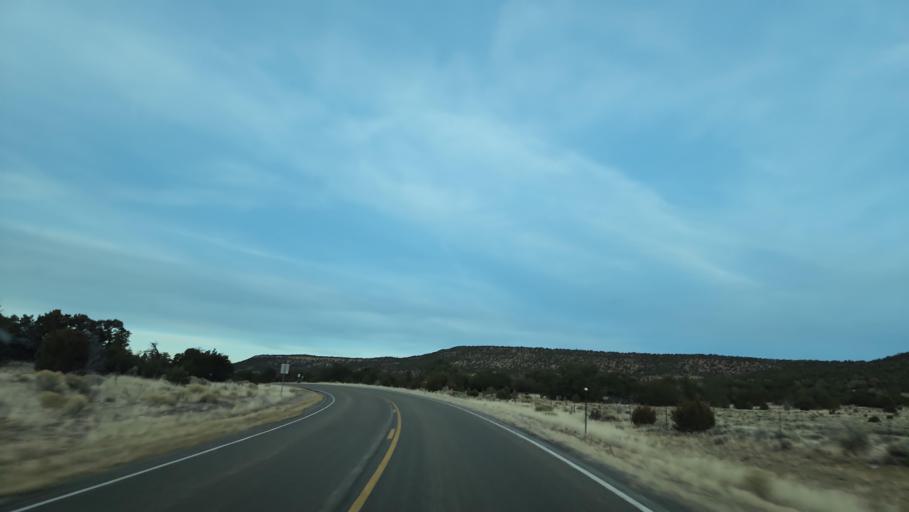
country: US
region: New Mexico
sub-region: Cibola County
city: Grants
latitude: 34.7322
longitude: -107.9669
